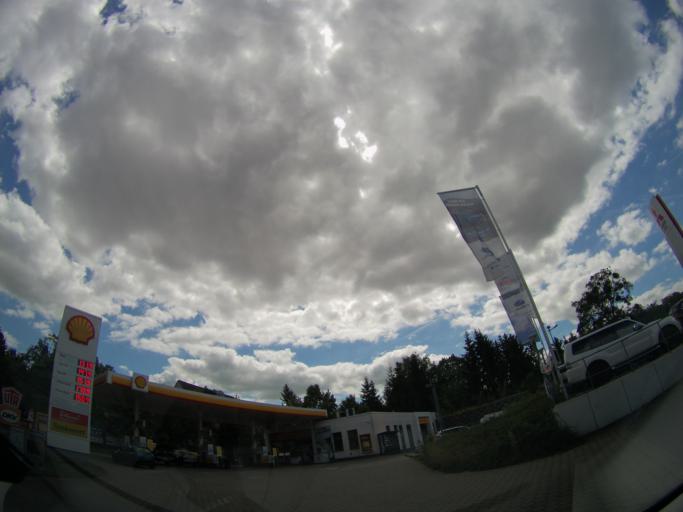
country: DE
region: Brandenburg
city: Stahnsdorf
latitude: 52.3935
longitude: 13.2186
